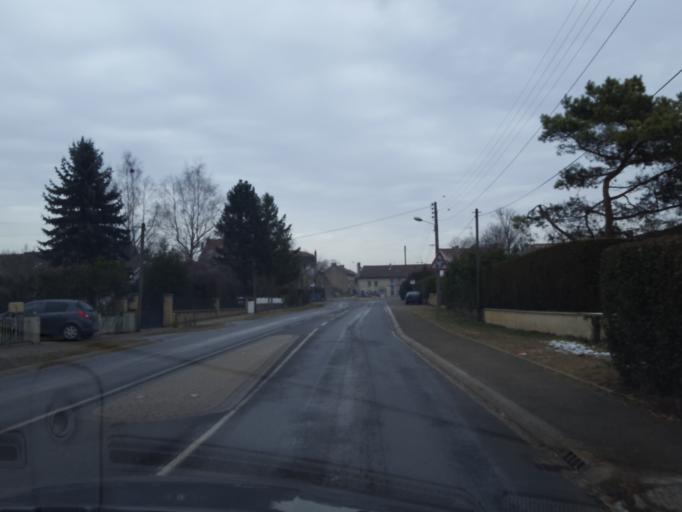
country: FR
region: Lorraine
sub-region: Departement de la Moselle
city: Chatel-Saint-Germain
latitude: 49.1142
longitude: 6.0272
